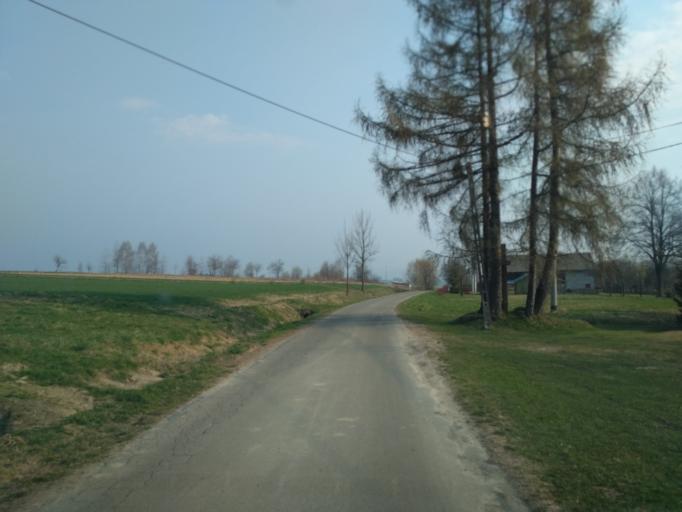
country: PL
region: Subcarpathian Voivodeship
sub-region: Powiat ropczycko-sedziszowski
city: Wielopole Skrzynskie
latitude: 49.9093
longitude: 21.5990
